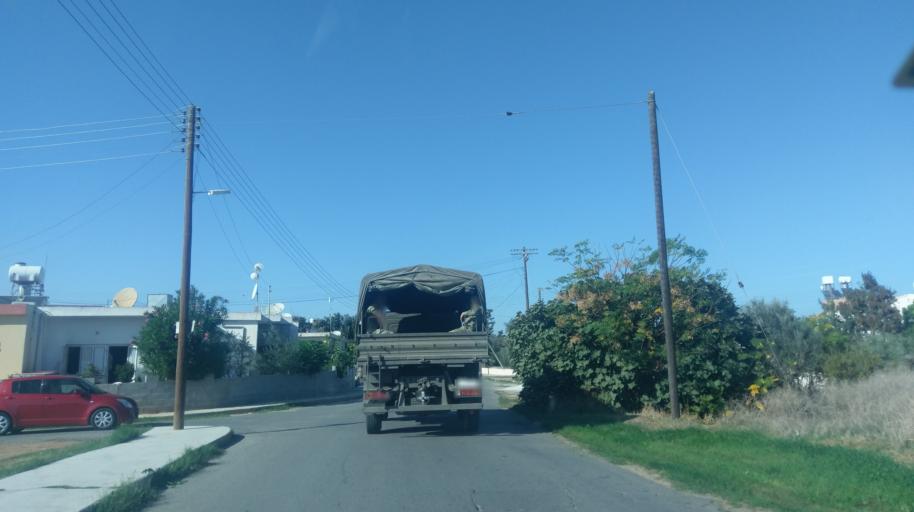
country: CY
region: Ammochostos
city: Famagusta
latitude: 35.1017
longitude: 33.9481
